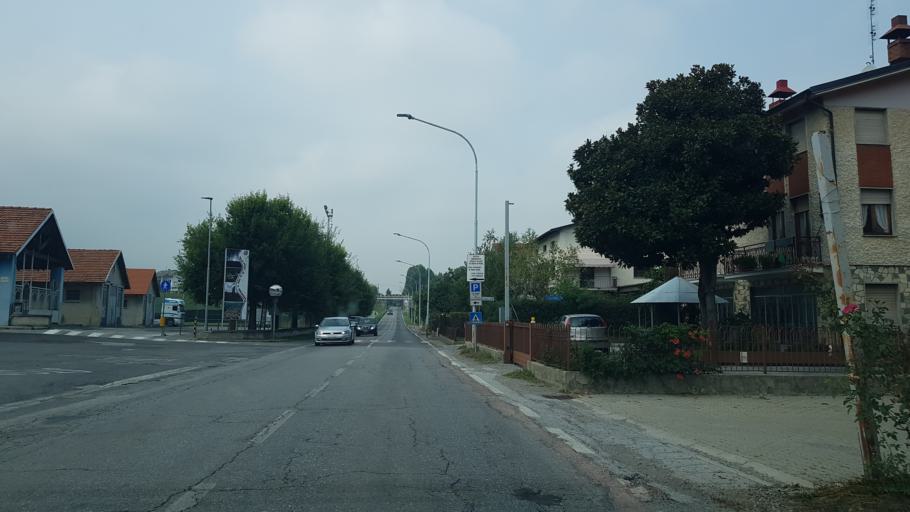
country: IT
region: Piedmont
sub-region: Provincia di Cuneo
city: Chiusa di Pesio
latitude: 44.3275
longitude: 7.6761
